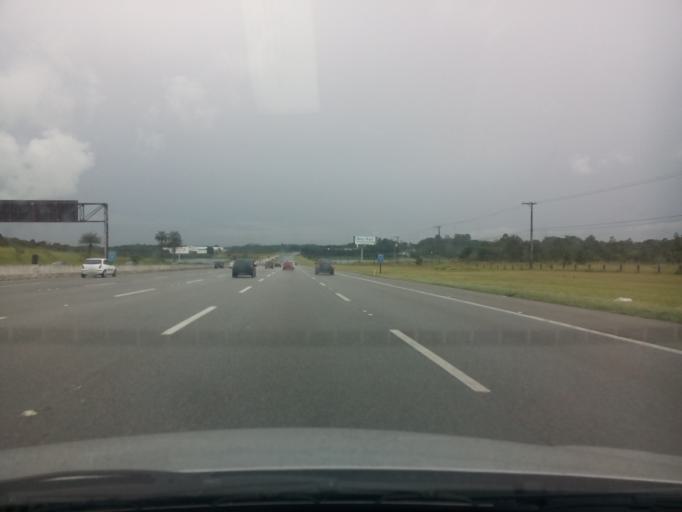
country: BR
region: Sao Paulo
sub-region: Sao Bernardo Do Campo
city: Sao Bernardo do Campo
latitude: -23.8015
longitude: -46.5903
